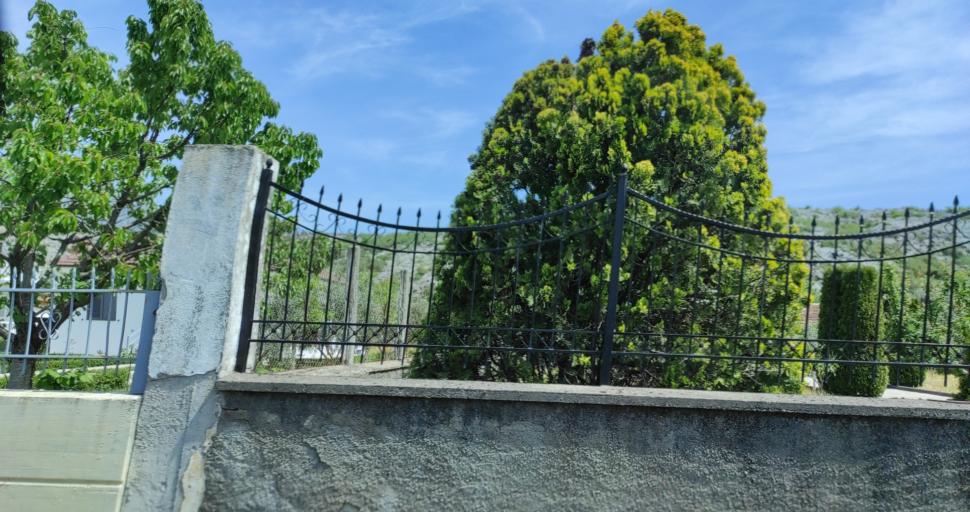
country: AL
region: Shkoder
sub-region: Rrethi i Malesia e Madhe
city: Gruemire
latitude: 42.1248
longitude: 19.5569
